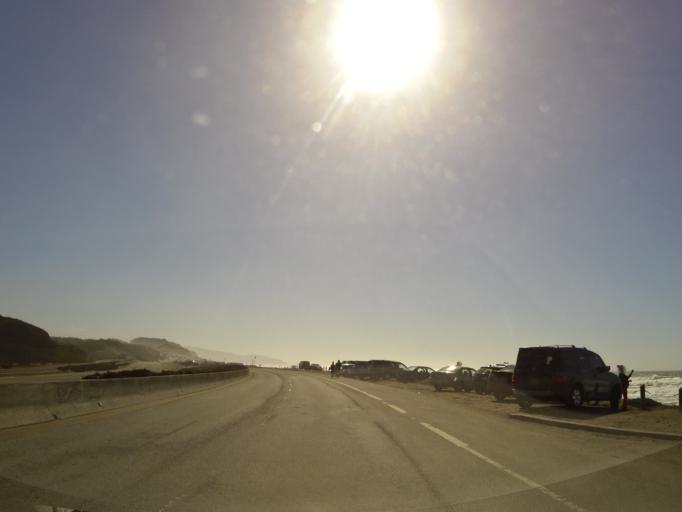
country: US
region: California
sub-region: San Mateo County
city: Broadmoor
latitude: 37.7334
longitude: -122.5072
